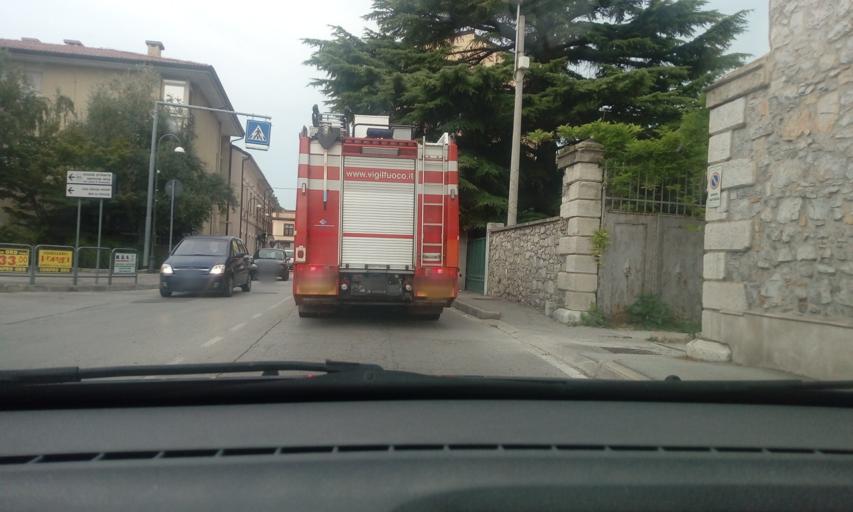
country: IT
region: Friuli Venezia Giulia
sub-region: Provincia di Gorizia
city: Ronchi dei Legionari
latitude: 45.8271
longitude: 13.5035
